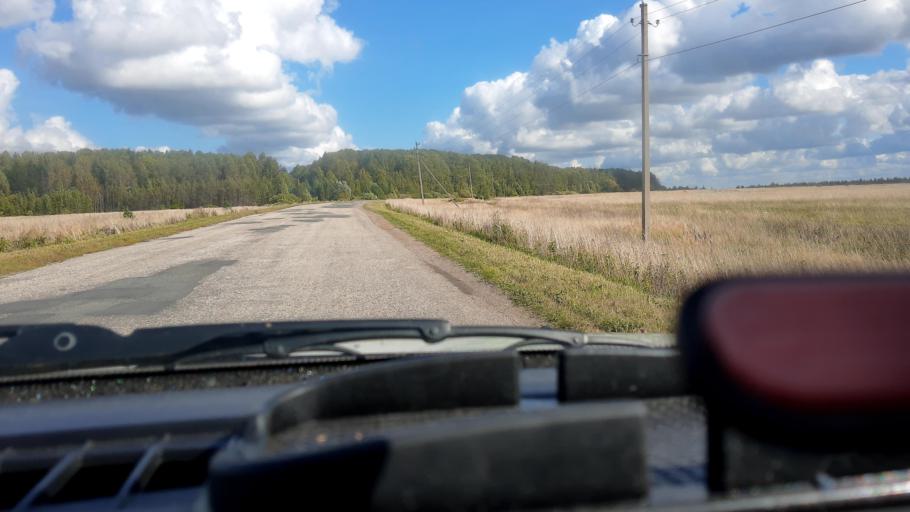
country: RU
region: Mariy-El
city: Kilemary
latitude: 56.9398
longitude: 46.6574
